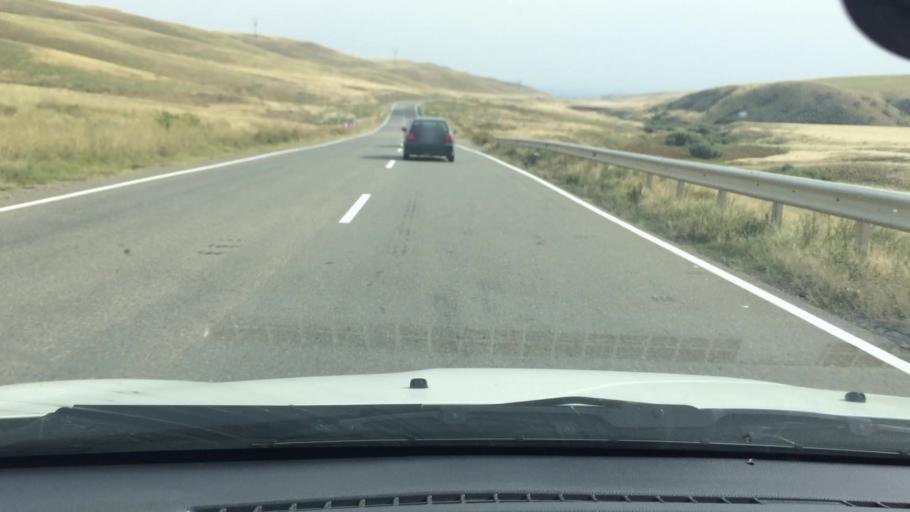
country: GE
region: Kvemo Kartli
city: Rust'avi
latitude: 41.5214
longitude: 44.9384
